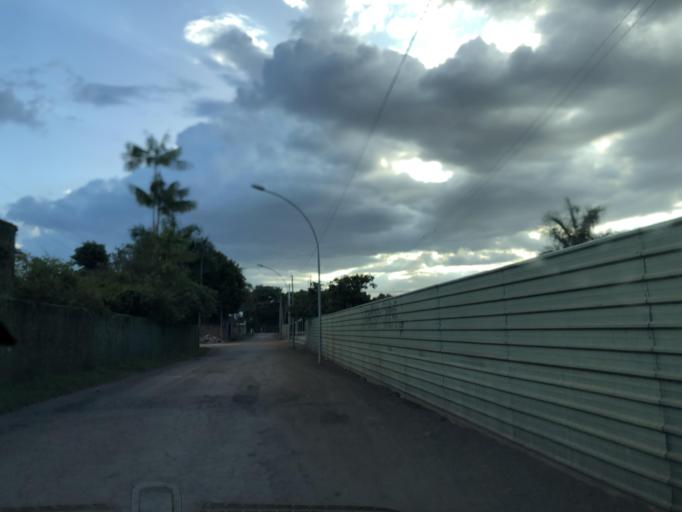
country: BR
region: Federal District
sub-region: Brasilia
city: Brasilia
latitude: -15.8765
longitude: -47.9725
